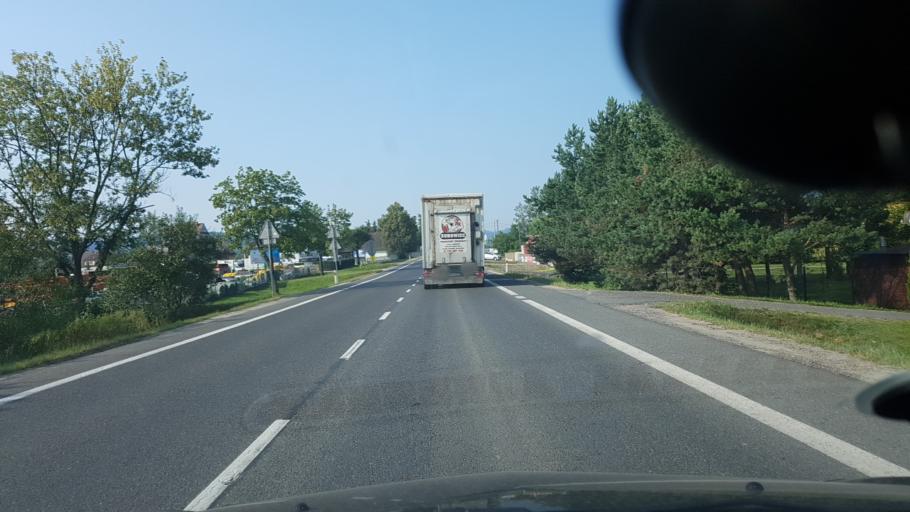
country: PL
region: Lesser Poland Voivodeship
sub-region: Powiat nowotarski
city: Rokiciny
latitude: 49.6007
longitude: 19.9223
